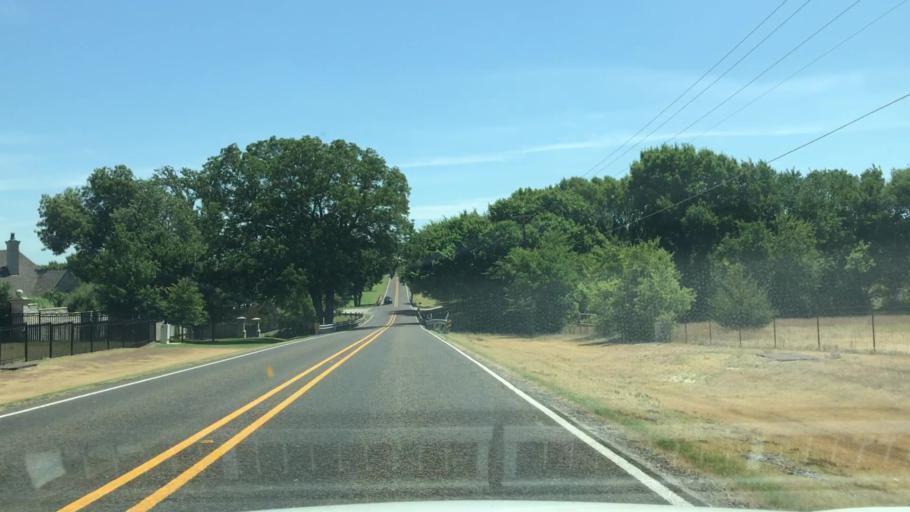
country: US
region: Texas
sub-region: Collin County
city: Fairview
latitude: 33.1563
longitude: -96.6230
